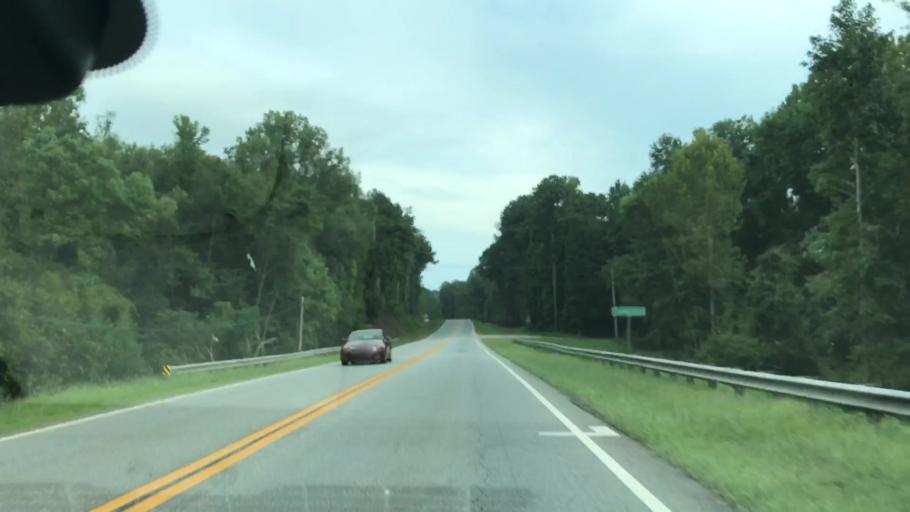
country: US
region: Georgia
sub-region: Quitman County
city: Georgetown
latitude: 31.8758
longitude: -85.0814
